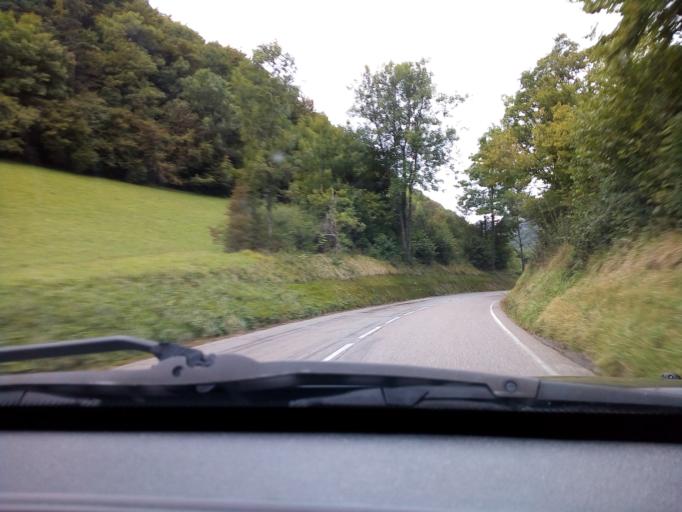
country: FR
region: Rhone-Alpes
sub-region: Departement de l'Isere
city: Corenc
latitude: 45.2348
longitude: 5.7510
